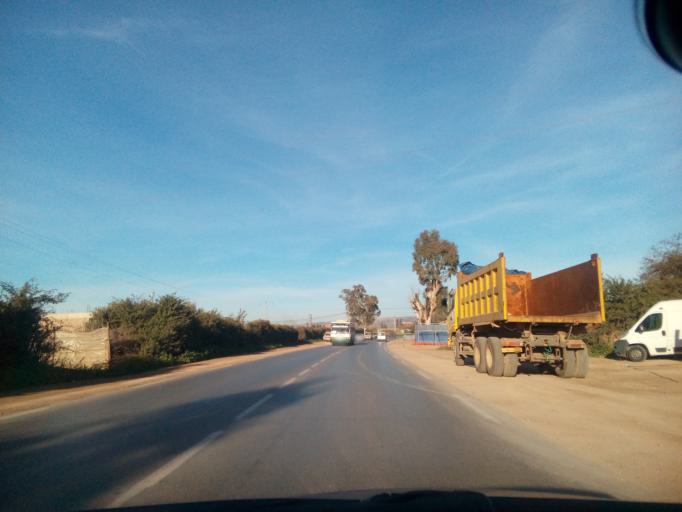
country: DZ
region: Mostaganem
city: Mostaganem
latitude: 35.7854
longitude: 0.1786
